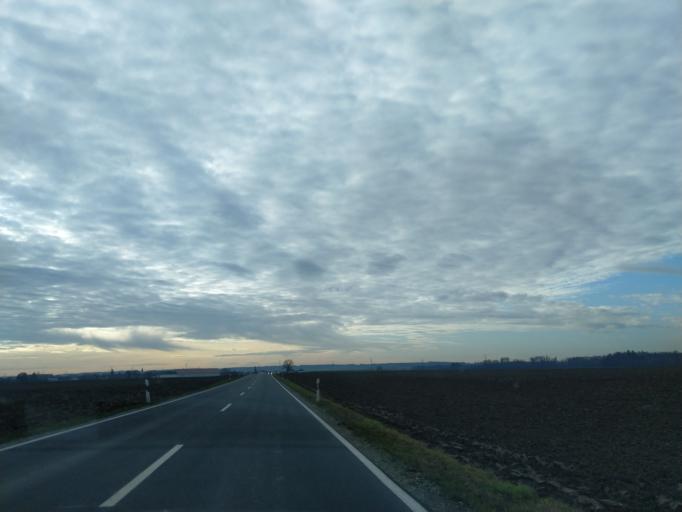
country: DE
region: Bavaria
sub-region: Lower Bavaria
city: Aholming
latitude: 48.7273
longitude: 12.9404
